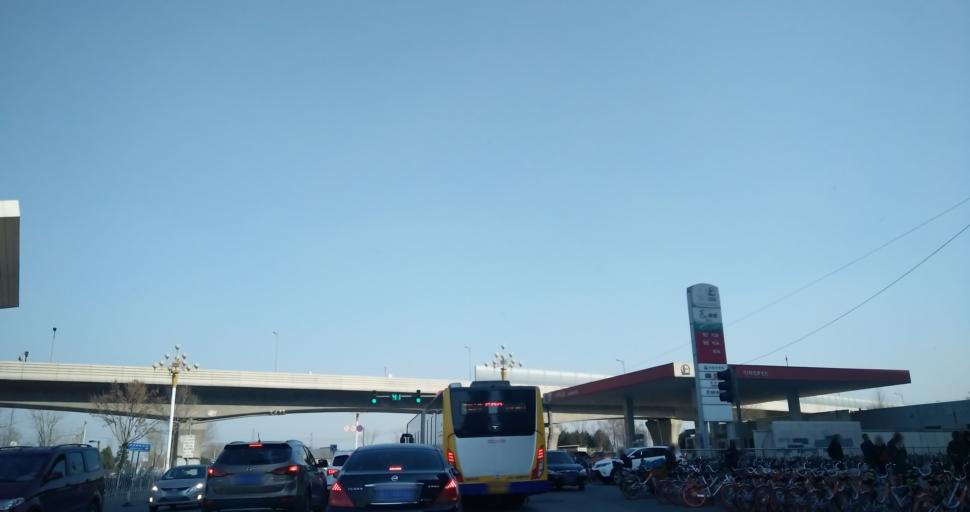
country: CN
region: Beijing
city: Jiugong
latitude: 39.8048
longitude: 116.4540
